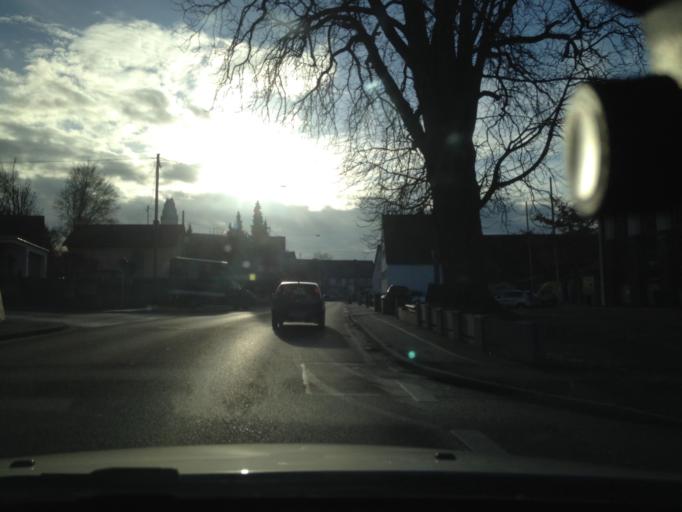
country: DE
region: Bavaria
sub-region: Swabia
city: Grossaitingen
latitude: 48.2311
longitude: 10.7837
